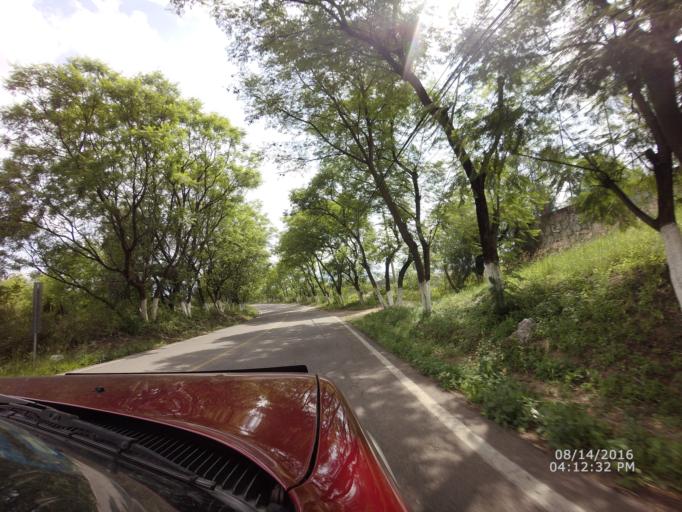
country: MX
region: Oaxaca
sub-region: San Lorenzo Cacaotepec
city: Santiago Etla
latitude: 17.1773
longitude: -96.7764
